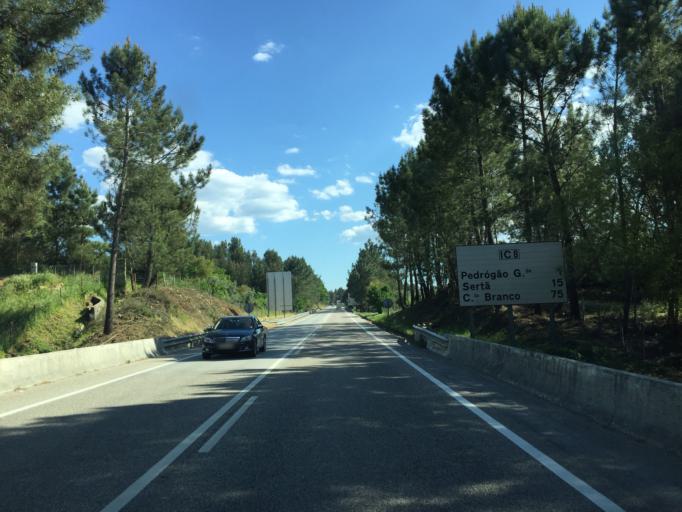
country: PT
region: Leiria
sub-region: Pedrogao Grande
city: Pedrogao Grande
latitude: 39.9180
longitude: -8.1538
